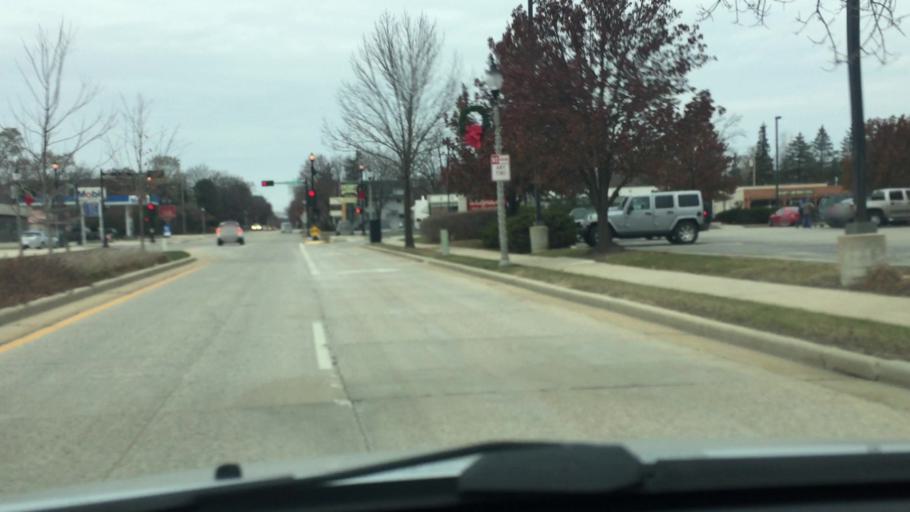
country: US
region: Wisconsin
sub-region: Ozaukee County
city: Mequon
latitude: 43.2354
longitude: -87.9840
